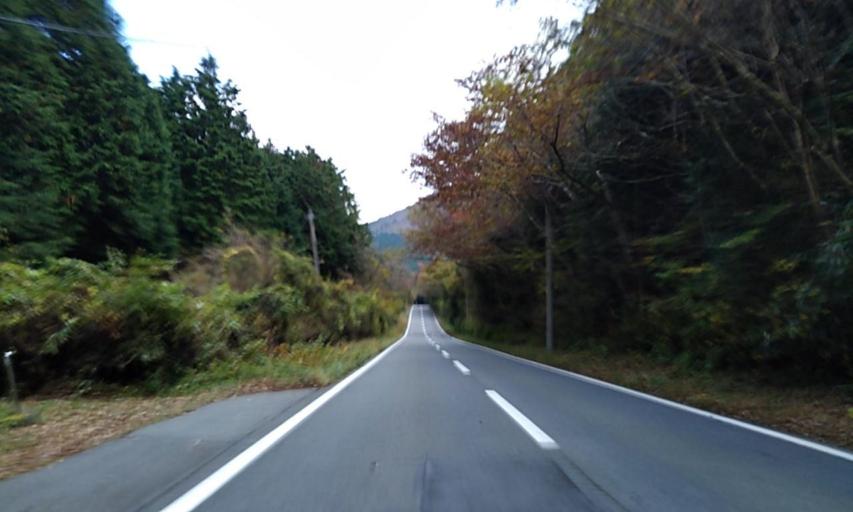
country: JP
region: Shizuoka
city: Gotemba
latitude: 35.2638
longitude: 138.8077
